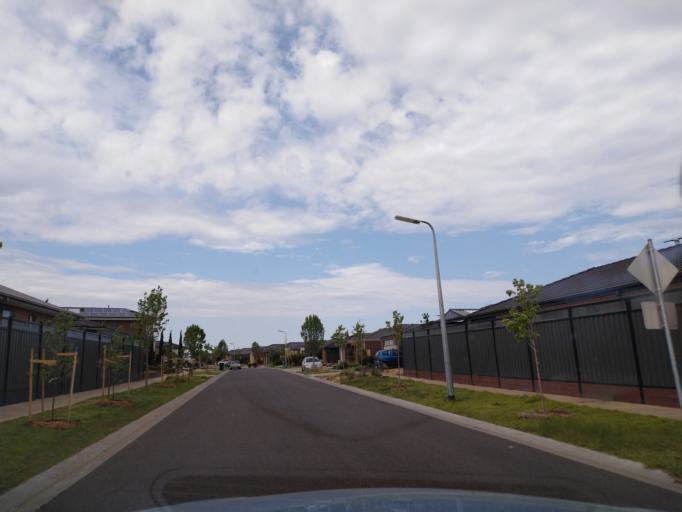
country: AU
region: Victoria
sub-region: Wyndham
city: Williams Landing
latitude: -37.8438
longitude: 144.7144
